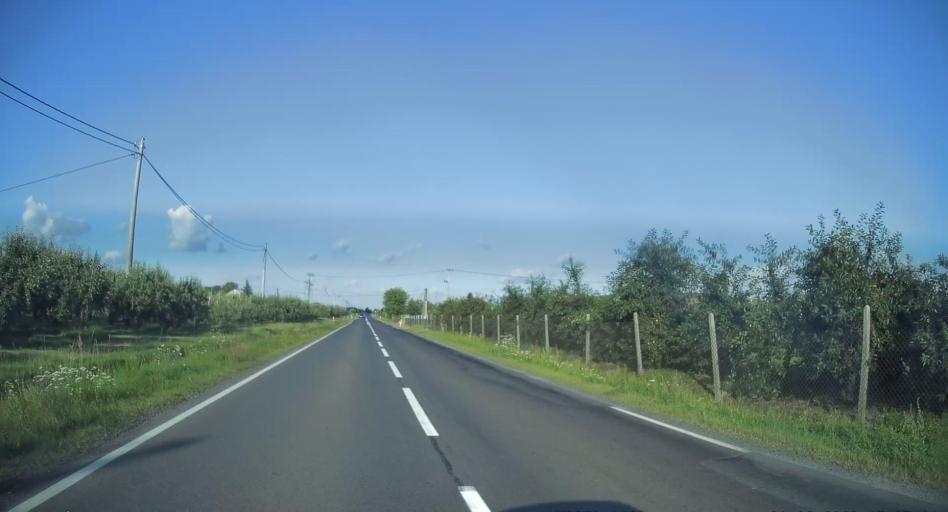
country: PL
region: Masovian Voivodeship
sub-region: Powiat grojecki
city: Bledow
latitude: 51.8023
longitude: 20.6351
